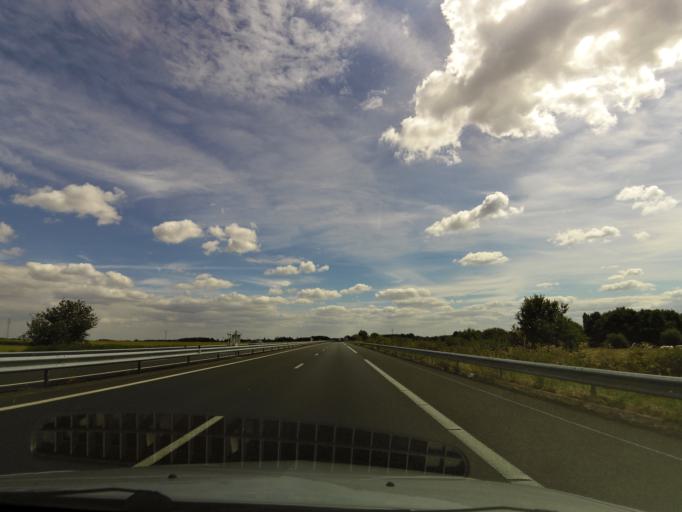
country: FR
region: Pays de la Loire
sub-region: Departement de la Vendee
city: Les Brouzils
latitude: 46.8906
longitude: -1.2961
